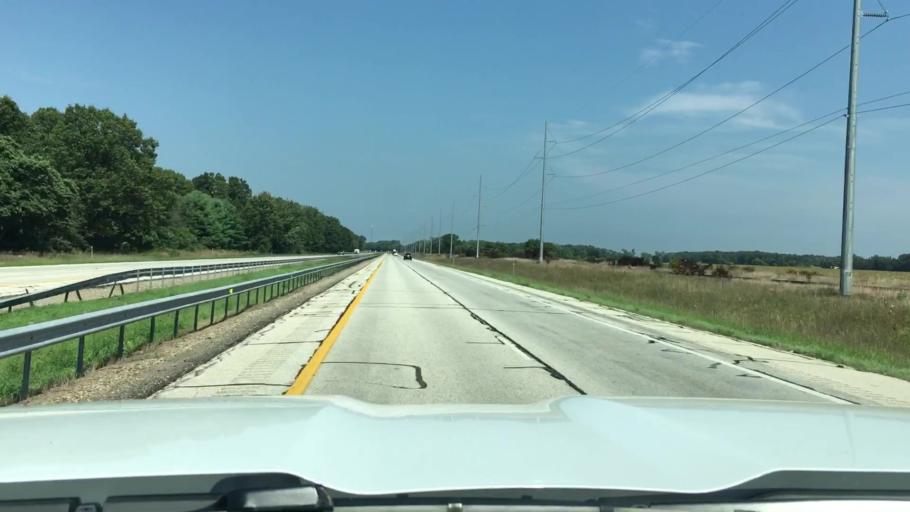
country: US
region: Michigan
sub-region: Saint Joseph County
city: Three Rivers
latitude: 42.0008
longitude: -85.6334
